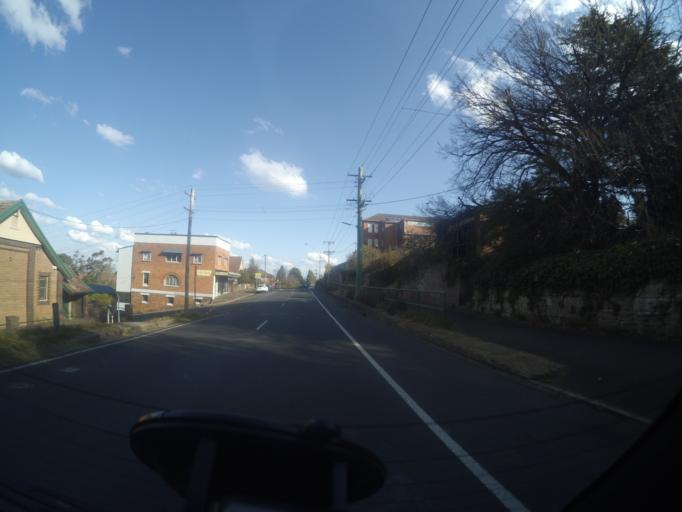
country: AU
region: New South Wales
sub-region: Blue Mountains Municipality
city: Katoomba
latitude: -33.7151
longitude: 150.3127
